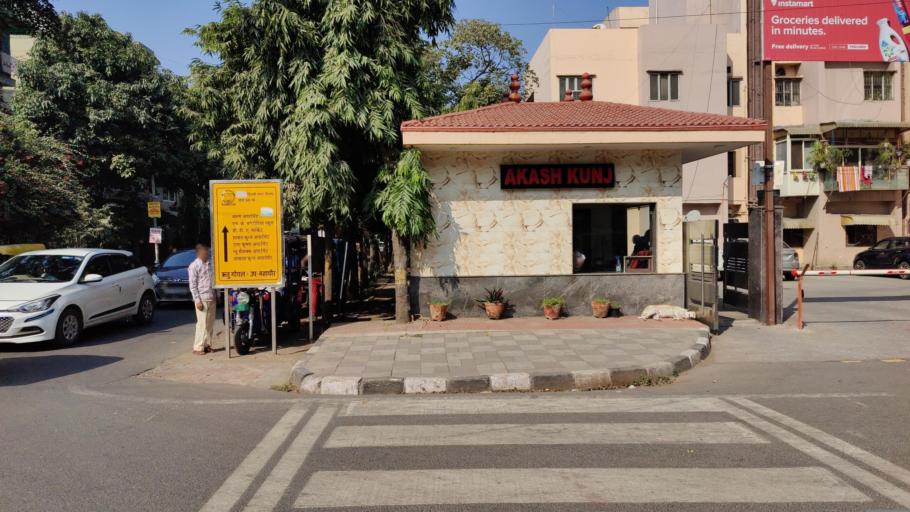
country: IN
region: NCT
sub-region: North West Delhi
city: Pitampura
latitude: 28.7117
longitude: 77.1275
